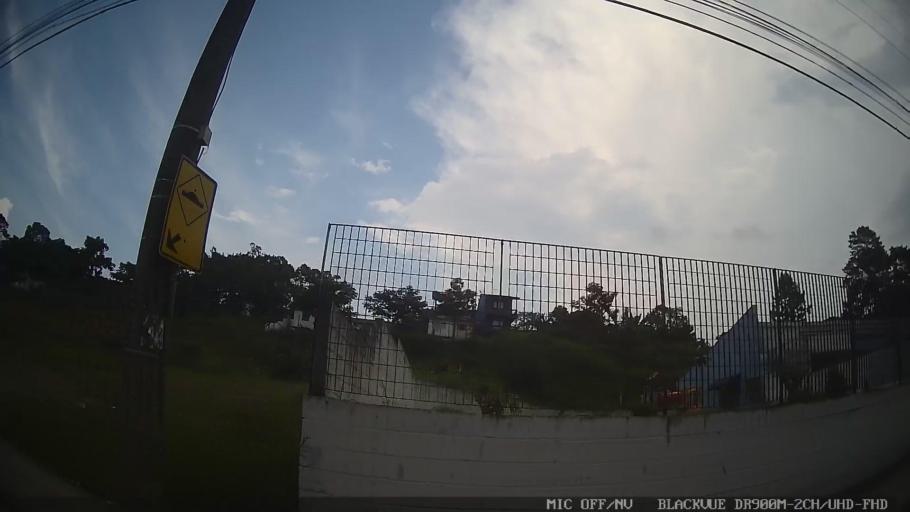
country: BR
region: Sao Paulo
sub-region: Ribeirao Pires
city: Ribeirao Pires
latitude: -23.6747
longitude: -46.3445
